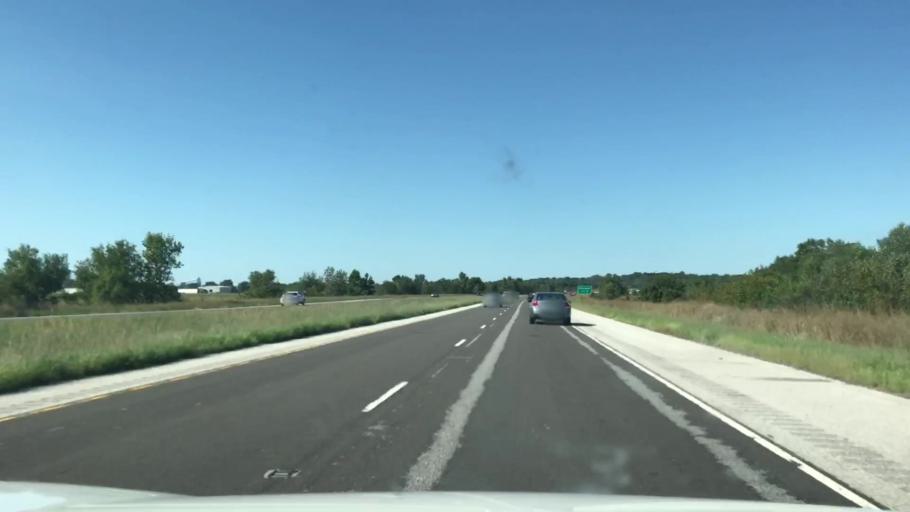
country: US
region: Illinois
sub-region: Madison County
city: South Roxana
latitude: 38.8230
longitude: -90.0429
